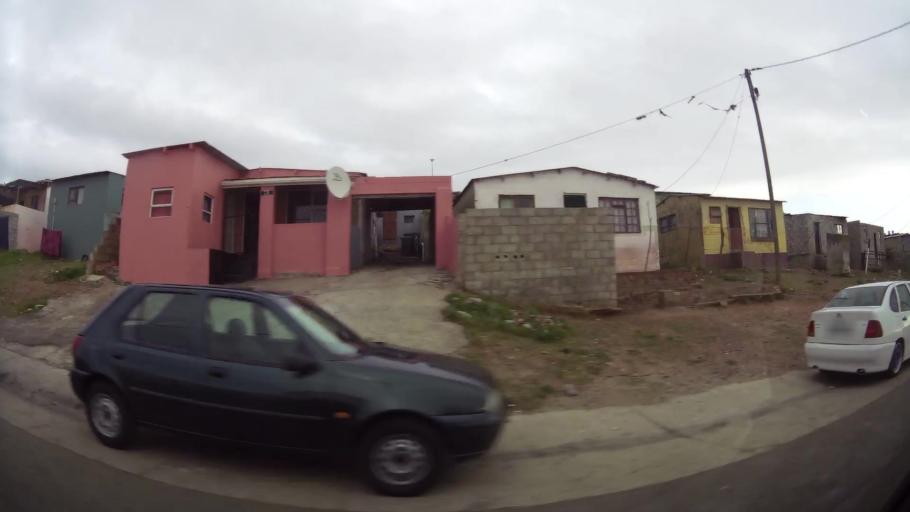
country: ZA
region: Eastern Cape
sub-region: Nelson Mandela Bay Metropolitan Municipality
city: Port Elizabeth
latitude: -33.9078
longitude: 25.5414
